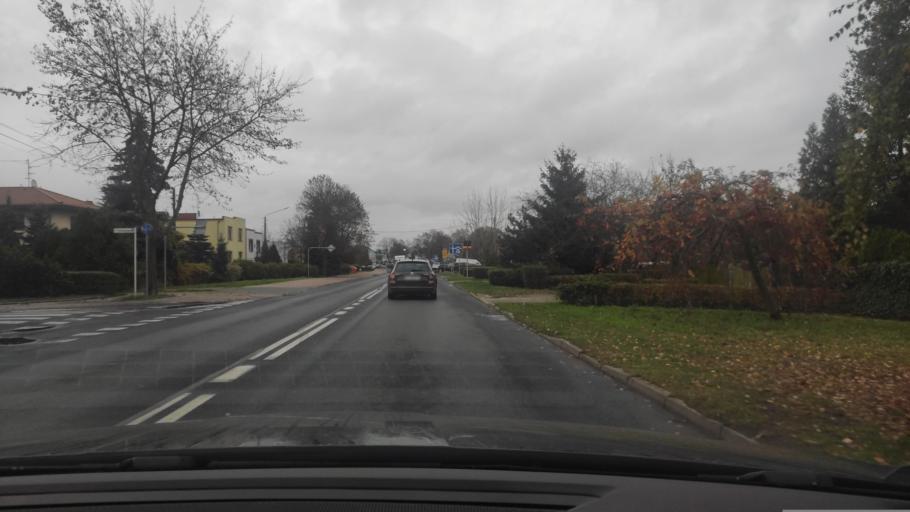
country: PL
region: Greater Poland Voivodeship
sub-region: Powiat poznanski
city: Kostrzyn
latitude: 52.3976
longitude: 17.2151
